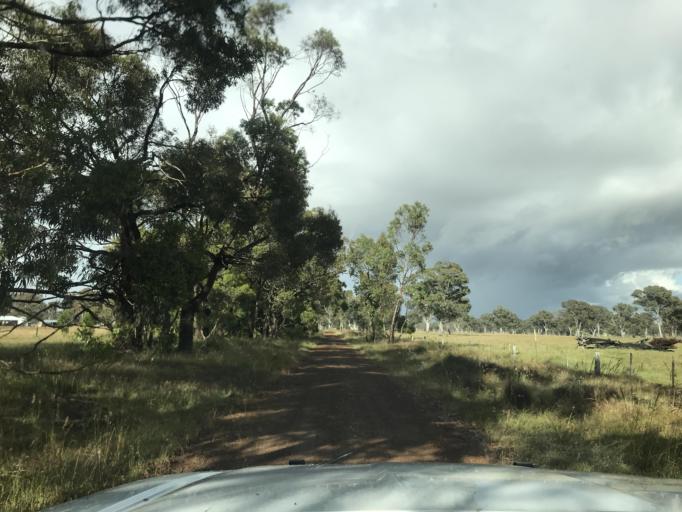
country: AU
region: South Australia
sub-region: Wattle Range
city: Penola
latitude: -37.1796
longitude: 141.3128
